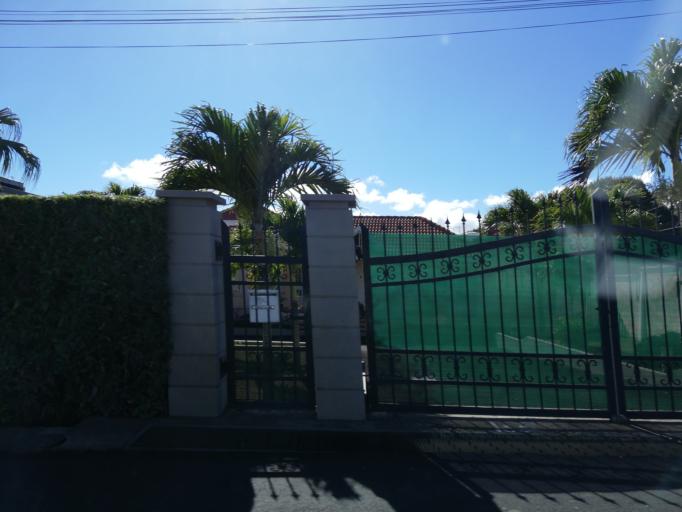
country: MU
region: Plaines Wilhems
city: Ebene
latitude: -20.2331
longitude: 57.4719
